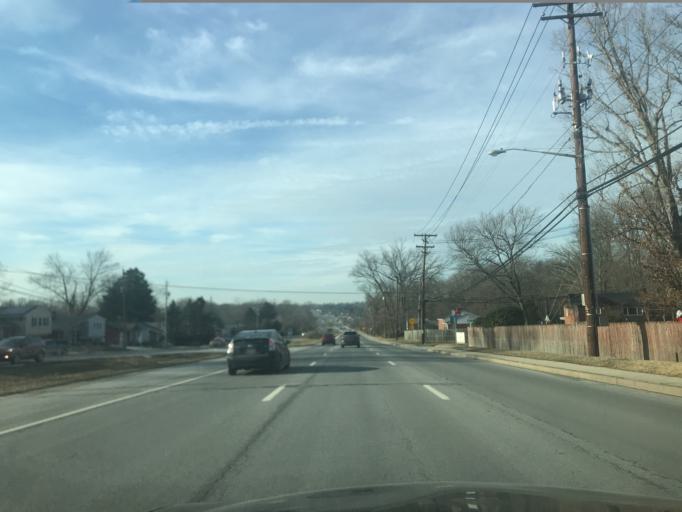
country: US
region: Maryland
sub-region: Montgomery County
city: Aspen Hill
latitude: 39.0734
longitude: -77.0657
